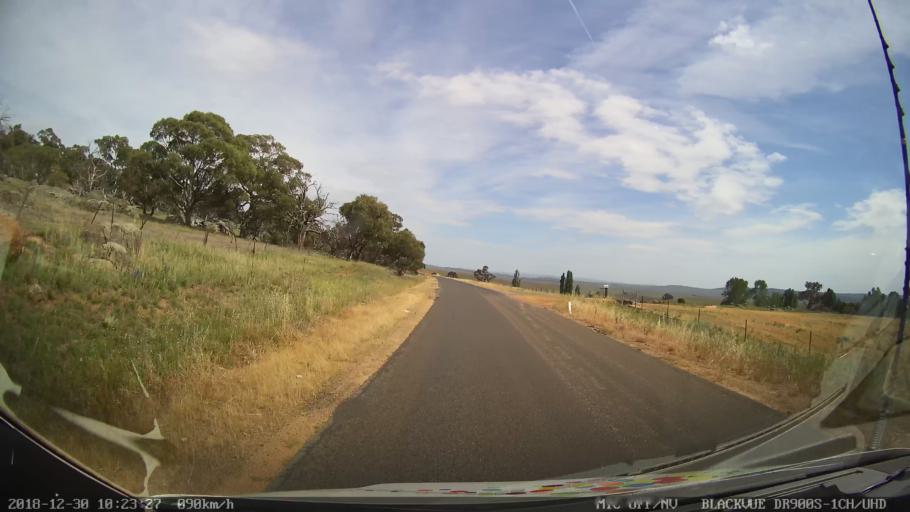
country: AU
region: New South Wales
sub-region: Snowy River
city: Berridale
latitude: -36.5372
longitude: 148.9819
